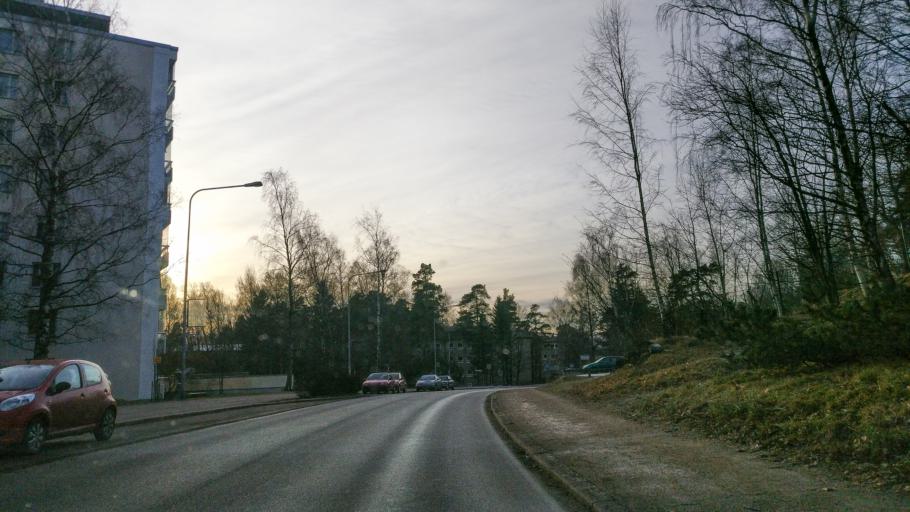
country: FI
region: Uusimaa
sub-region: Helsinki
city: Vantaa
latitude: 60.1995
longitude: 25.0588
